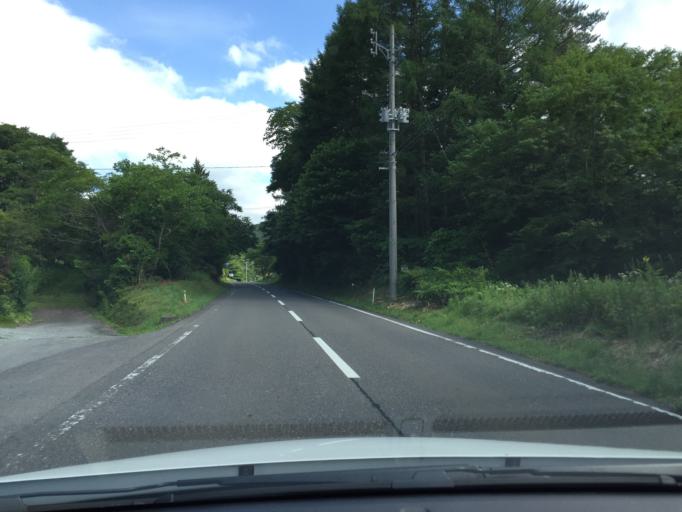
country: JP
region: Fukushima
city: Inawashiro
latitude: 37.2789
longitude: 140.0625
